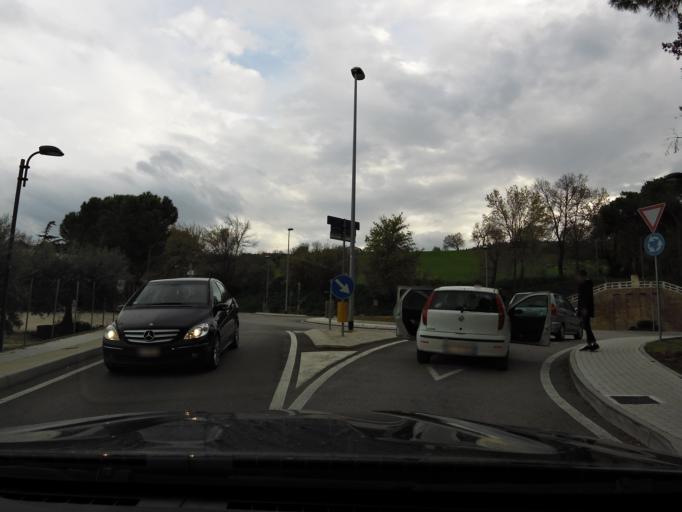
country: IT
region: The Marches
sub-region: Provincia di Ancona
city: Loreto Stazione
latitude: 43.4452
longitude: 13.6176
